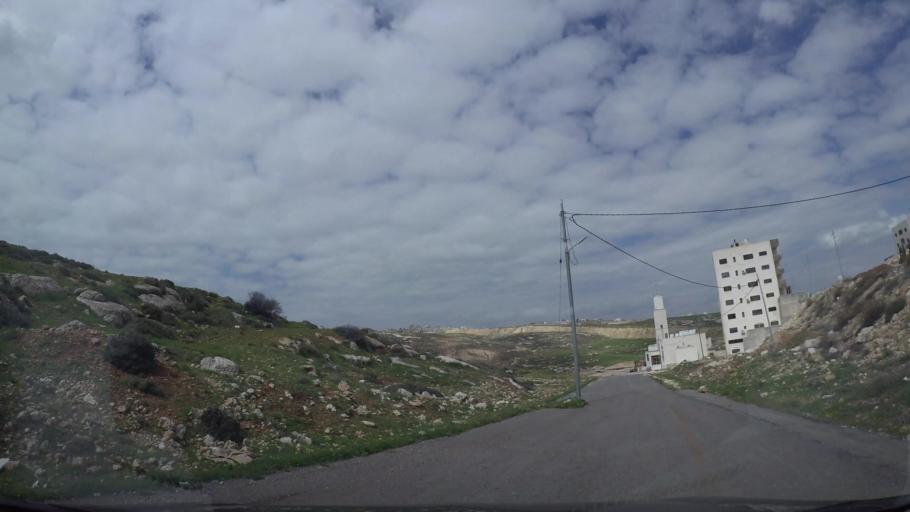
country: JO
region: Amman
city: Al Jubayhah
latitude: 32.0036
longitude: 35.9113
